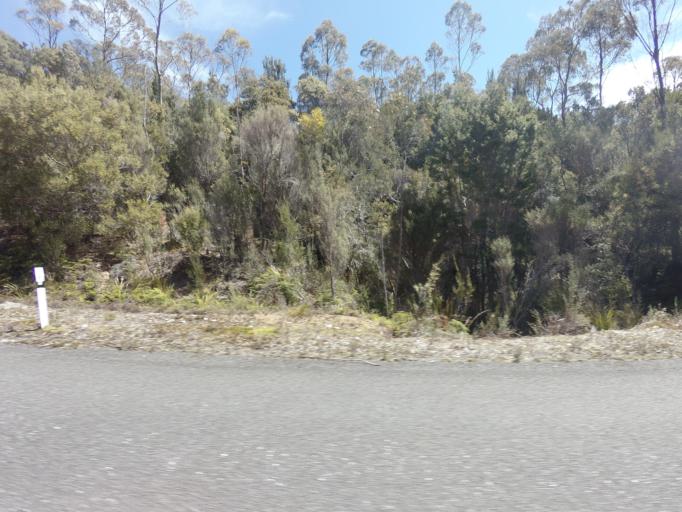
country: AU
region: Tasmania
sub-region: West Coast
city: Queenstown
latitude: -42.7721
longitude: 146.0428
